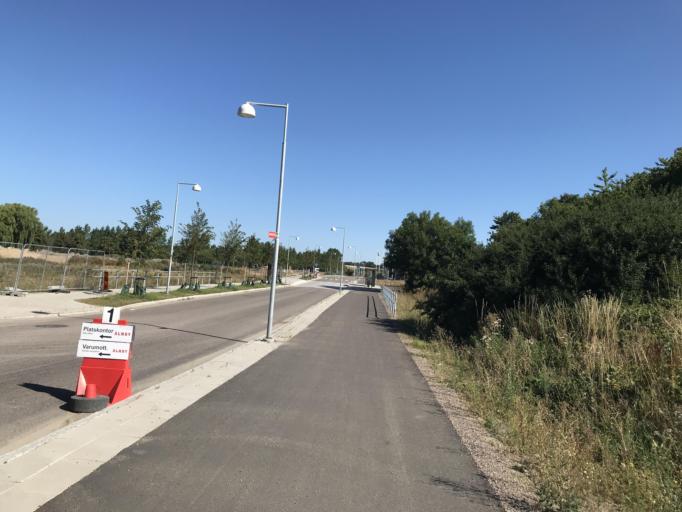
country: SE
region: Skane
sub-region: Landskrona
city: Landskrona
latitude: 55.9009
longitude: 12.8138
